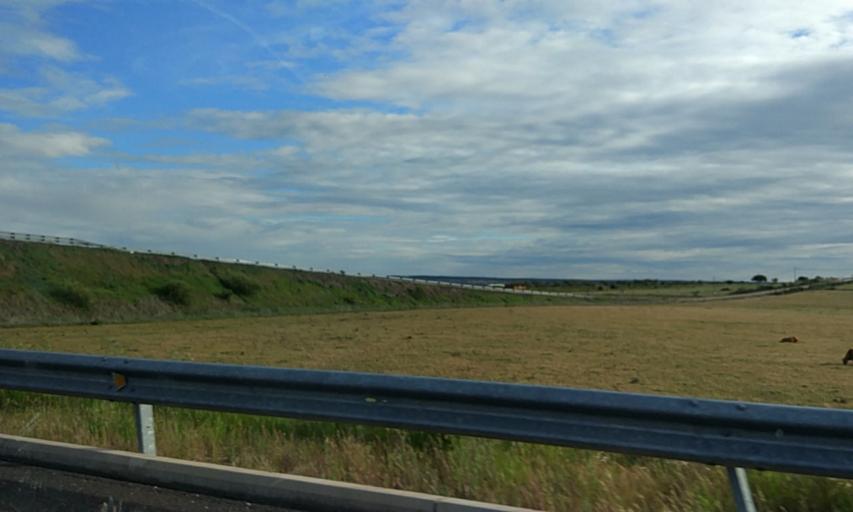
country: ES
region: Extremadura
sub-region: Provincia de Caceres
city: Casas de Don Gomez
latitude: 40.0167
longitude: -6.5871
